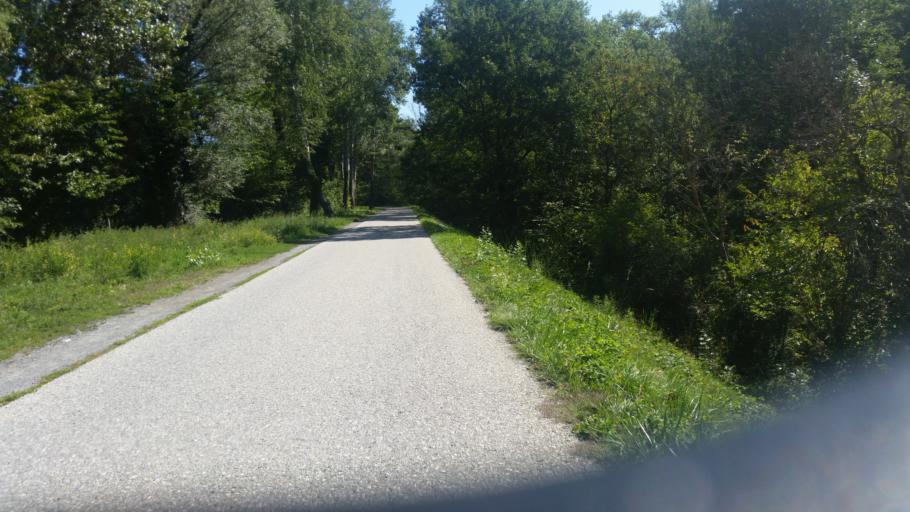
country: CH
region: Valais
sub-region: Sierre District
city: Chermignon-d'en Haut
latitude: 46.2710
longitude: 7.4837
